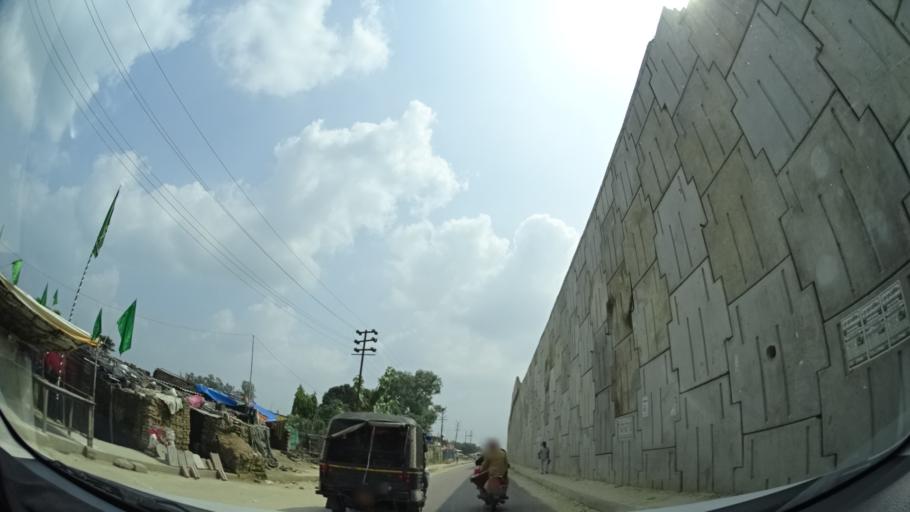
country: IN
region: Uttar Pradesh
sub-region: Maharajganj
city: Anandnagar
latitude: 27.0297
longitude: 83.2704
